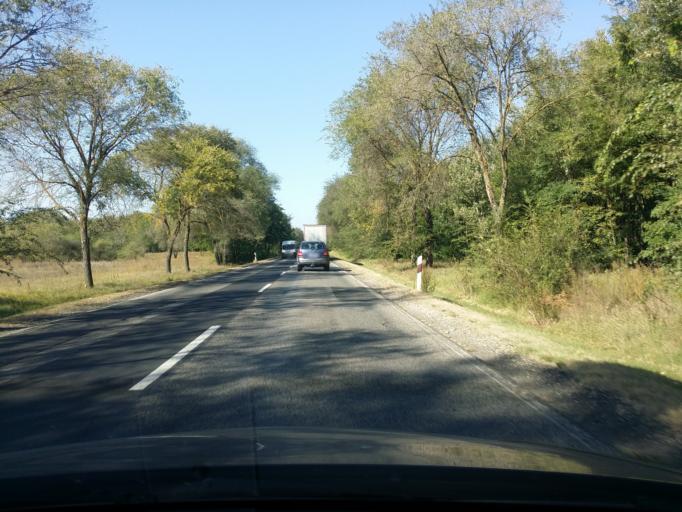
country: HU
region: Bacs-Kiskun
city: Nyarlorinc
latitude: 46.9023
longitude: 19.8169
